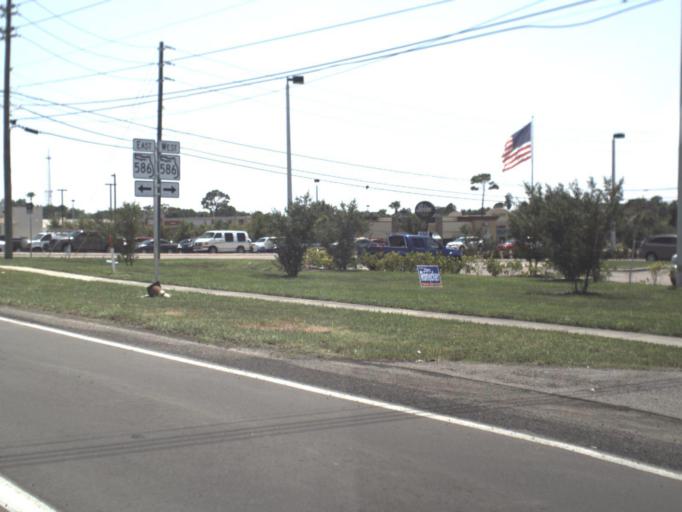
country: US
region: Florida
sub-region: Pinellas County
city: Saint George
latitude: 28.0496
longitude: -82.7388
